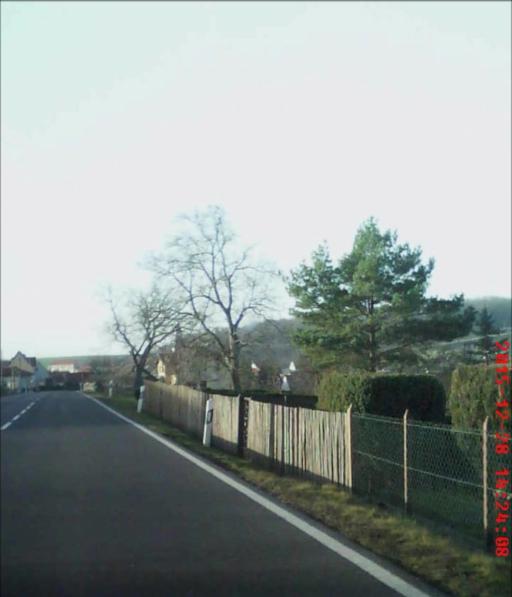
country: DE
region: Thuringia
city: Pfiffelbach
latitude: 51.0573
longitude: 11.4497
